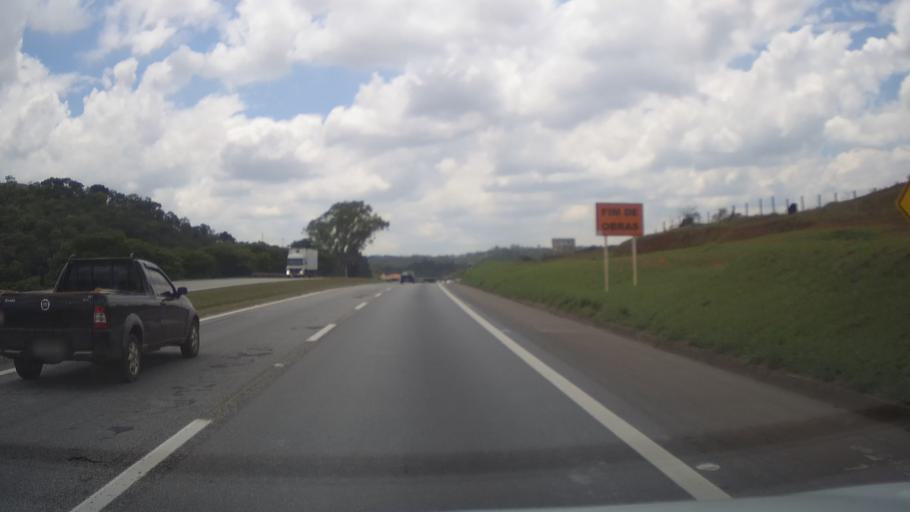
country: BR
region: Minas Gerais
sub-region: Tres Coracoes
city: Tres Coracoes
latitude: -21.6805
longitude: -45.3420
